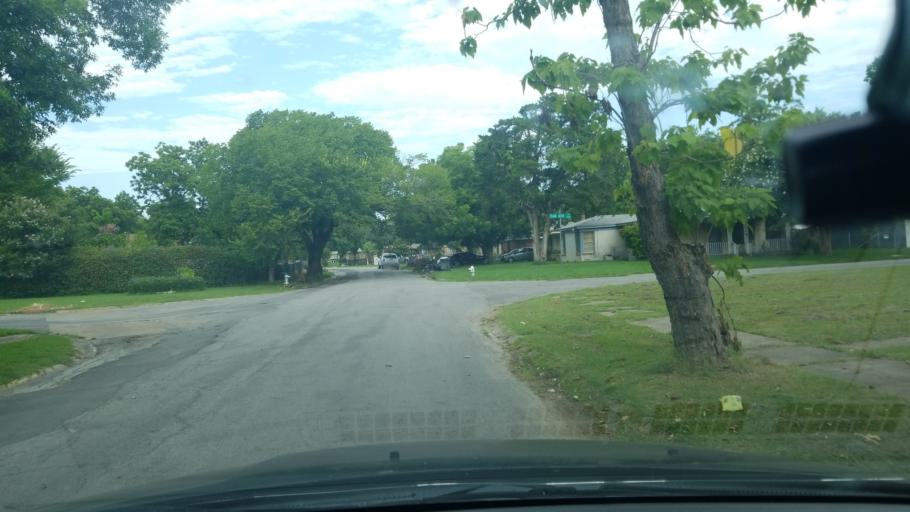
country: US
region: Texas
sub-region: Dallas County
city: Balch Springs
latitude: 32.7354
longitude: -96.6708
